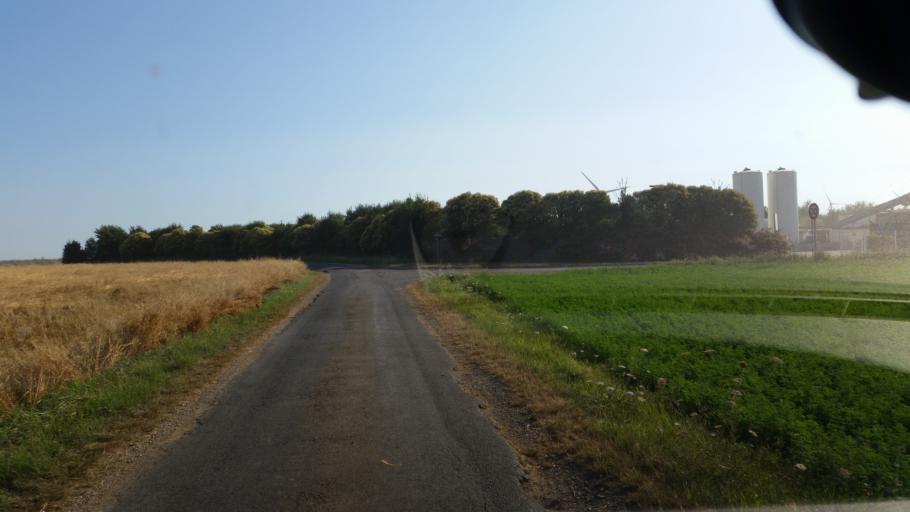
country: FR
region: Poitou-Charentes
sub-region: Departement de la Charente-Maritime
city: Saint-Jean-de-Liversay
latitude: 46.2334
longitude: -0.8895
